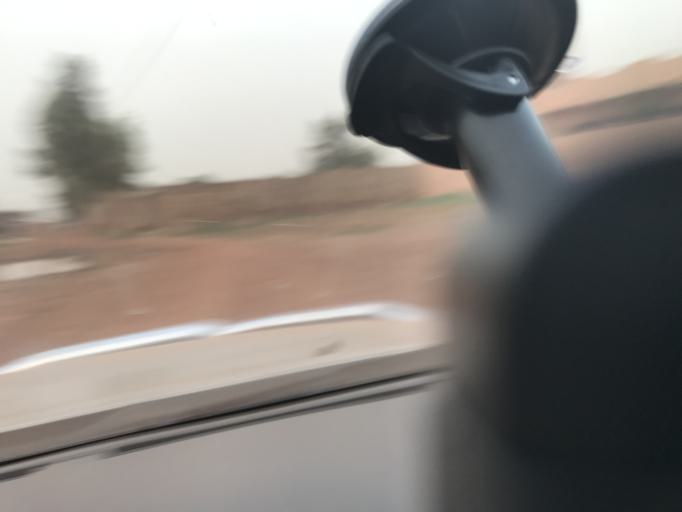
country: ML
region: Bamako
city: Bamako
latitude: 12.6531
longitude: -7.8847
